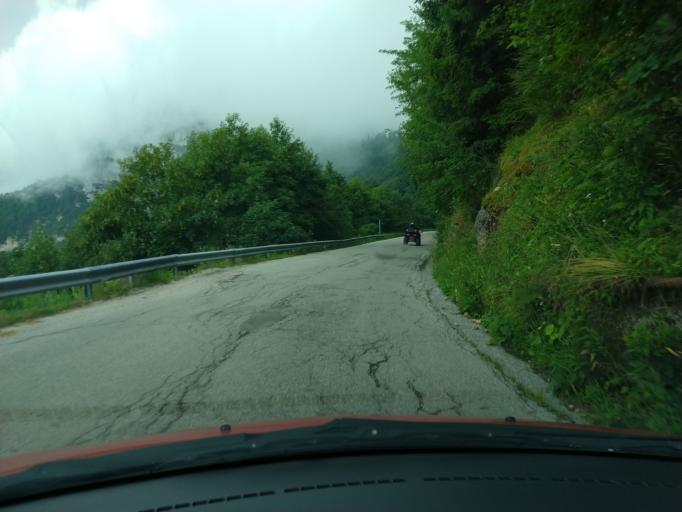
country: IT
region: Veneto
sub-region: Provincia di Vicenza
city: Longhi
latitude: 45.8779
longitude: 11.3045
